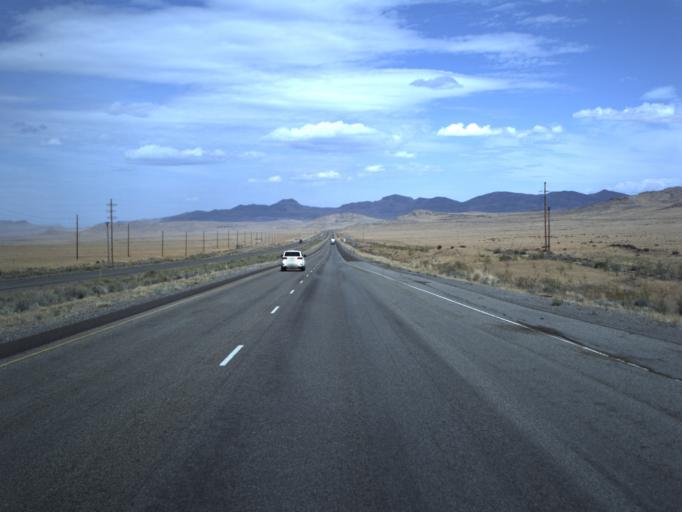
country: US
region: Utah
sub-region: Tooele County
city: Grantsville
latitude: 40.7731
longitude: -112.9773
